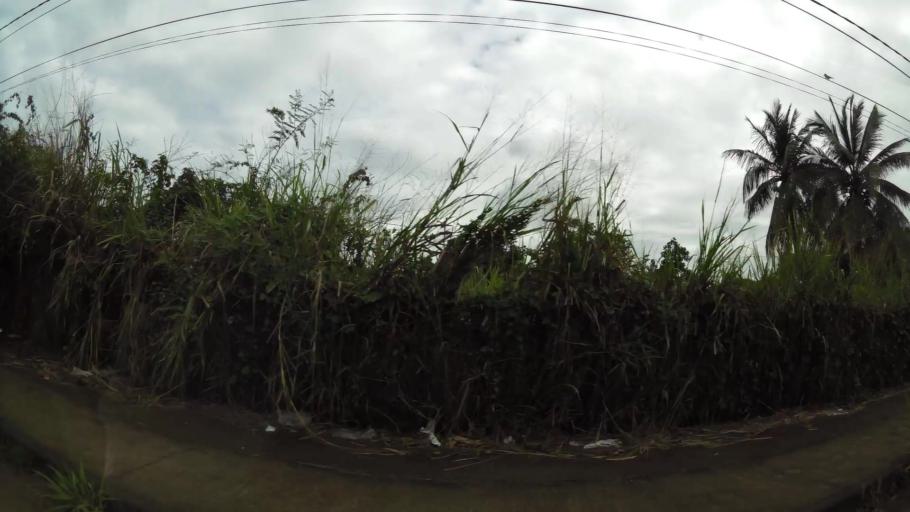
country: GP
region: Guadeloupe
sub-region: Guadeloupe
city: Sainte-Rose
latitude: 16.3258
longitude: -61.6943
